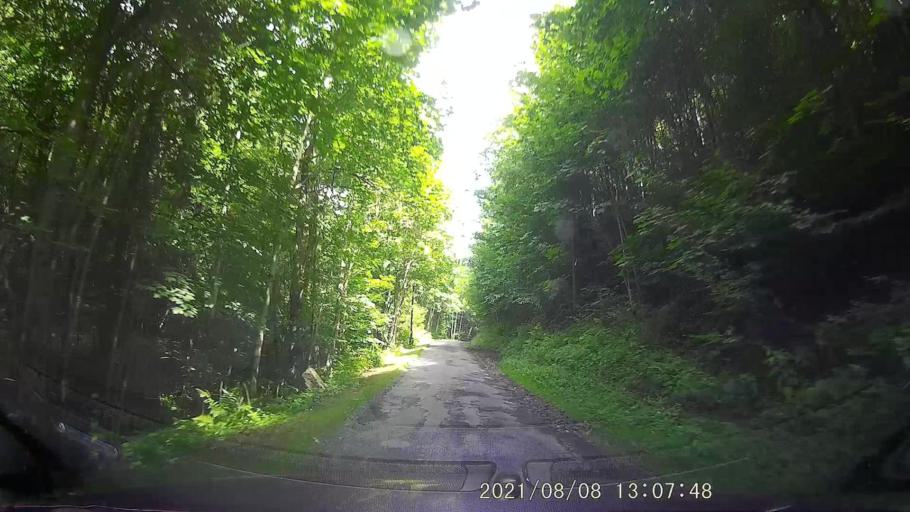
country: PL
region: Lower Silesian Voivodeship
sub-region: Powiat klodzki
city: Lewin Klodzki
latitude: 50.4349
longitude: 16.3008
